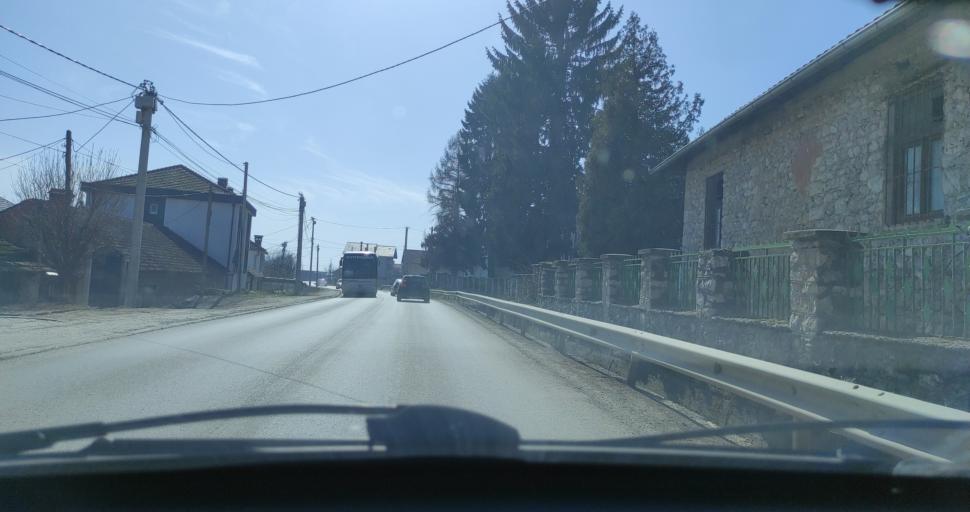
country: XK
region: Gjakova
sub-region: Komuna e Decanit
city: Strellc i Eperm
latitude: 42.5779
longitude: 20.2940
